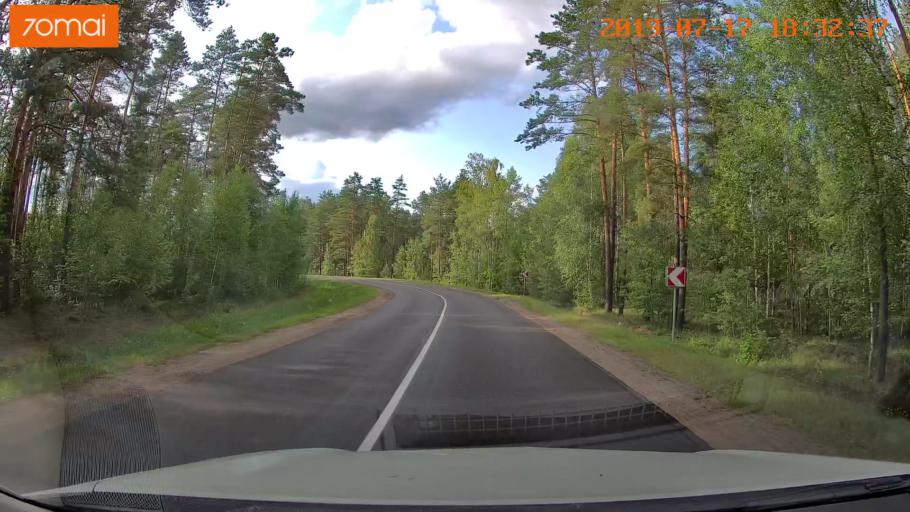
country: BY
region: Mogilev
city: Asipovichy
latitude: 53.2730
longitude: 28.6759
